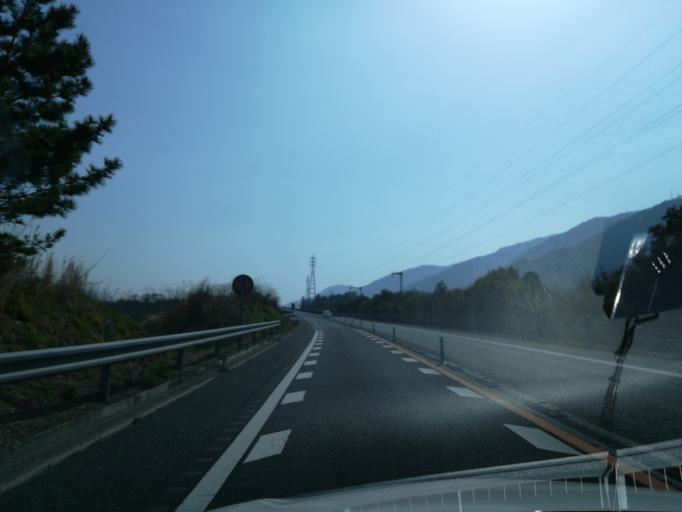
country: JP
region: Tokushima
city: Ikedacho
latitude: 34.0356
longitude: 133.8747
